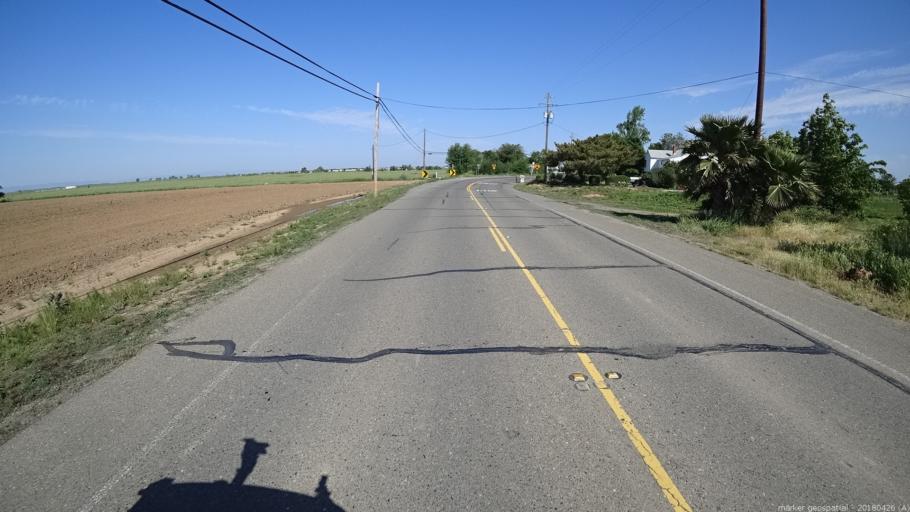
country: US
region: California
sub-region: Yolo County
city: West Sacramento
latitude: 38.5188
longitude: -121.5554
